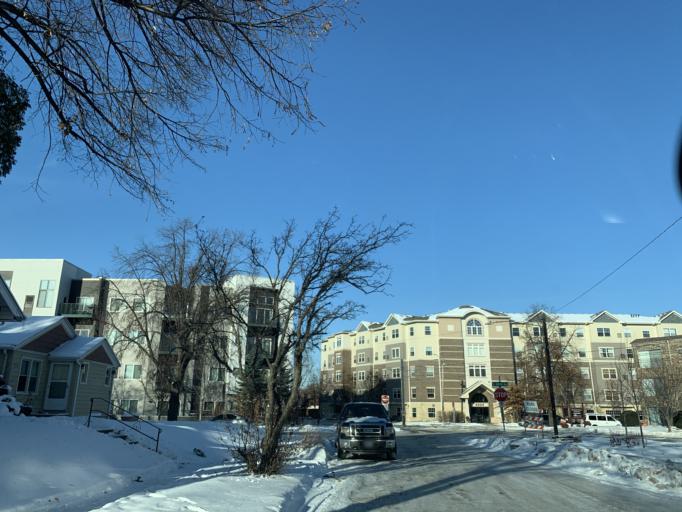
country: US
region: Minnesota
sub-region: Dakota County
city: Mendota Heights
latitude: 44.9068
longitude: -93.2050
